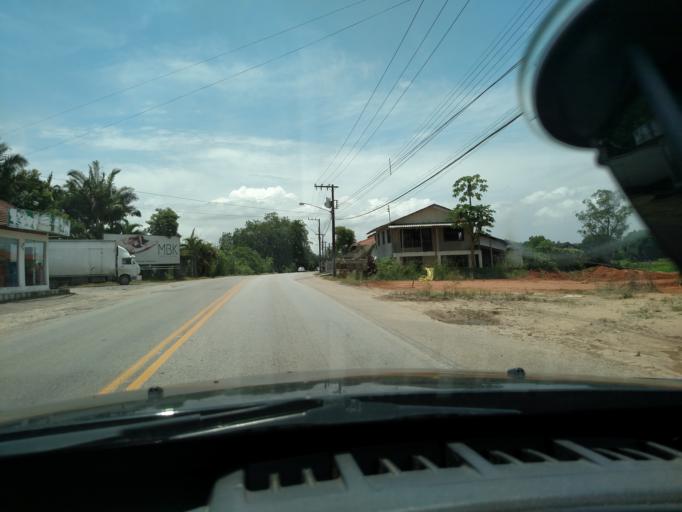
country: BR
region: Santa Catarina
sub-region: Gaspar
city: Gaspar
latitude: -26.9074
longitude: -48.8442
